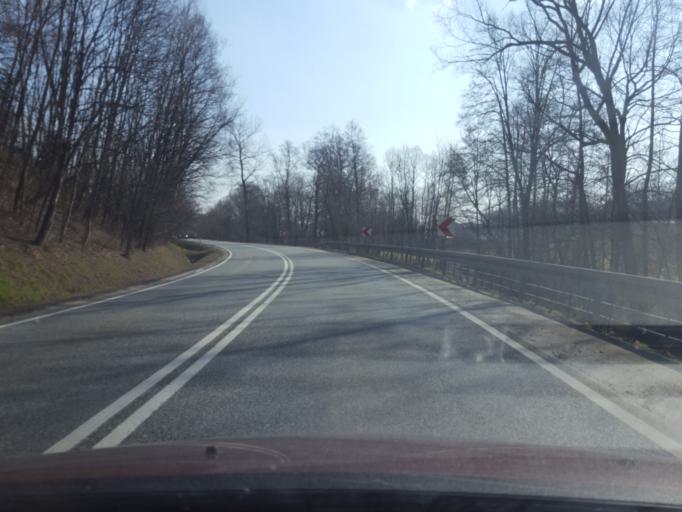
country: PL
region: Lesser Poland Voivodeship
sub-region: Powiat brzeski
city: Czchow
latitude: 49.8531
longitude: 20.6524
